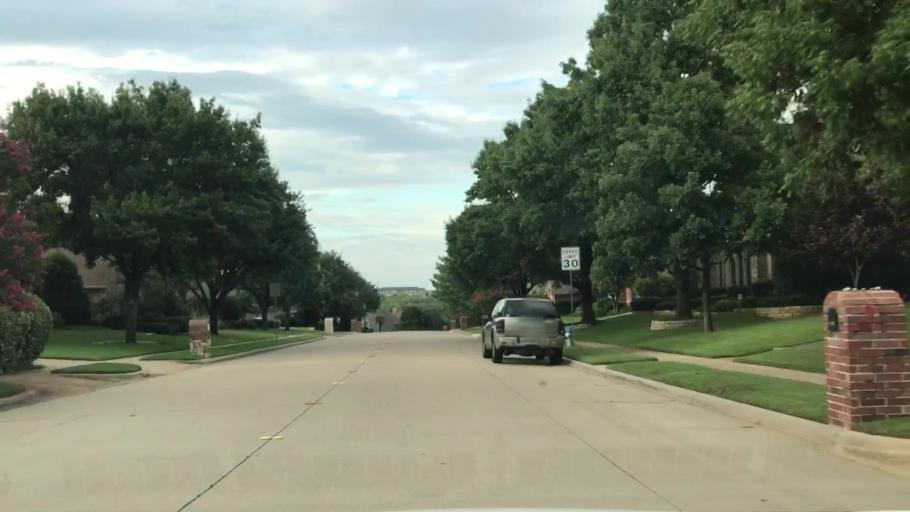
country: US
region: Texas
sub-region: Denton County
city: The Colony
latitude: 33.0407
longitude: -96.8501
